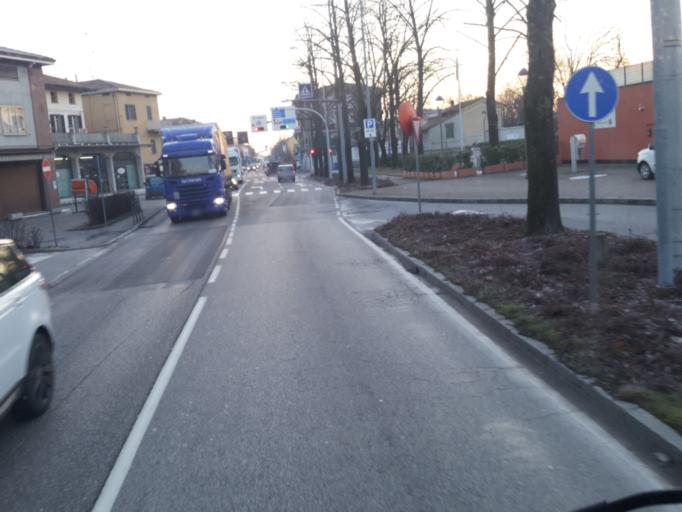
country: IT
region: Emilia-Romagna
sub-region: Provincia di Parma
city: Sorbolo
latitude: 44.8433
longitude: 10.4458
